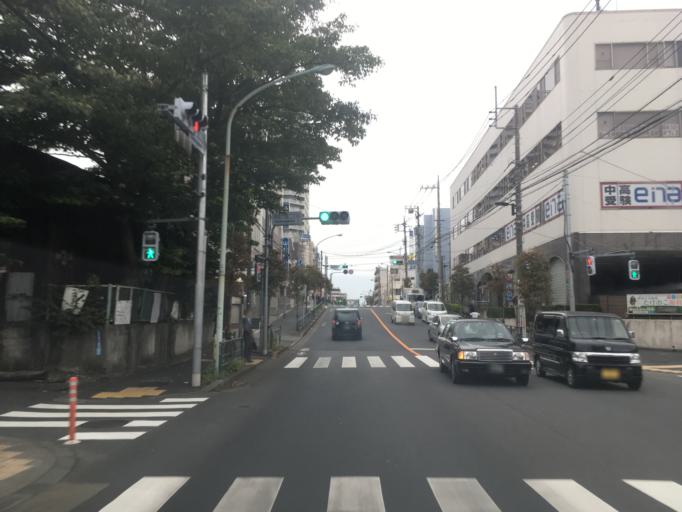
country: JP
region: Tokyo
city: Kokubunji
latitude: 35.7009
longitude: 139.4664
